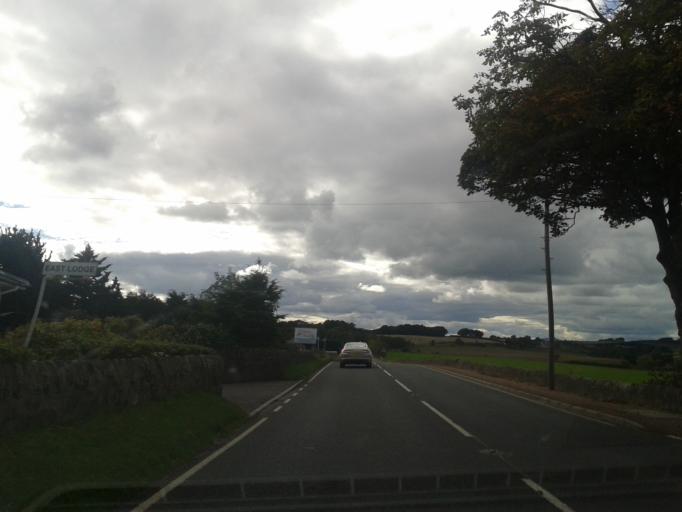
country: GB
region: Scotland
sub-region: Fife
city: Balmullo
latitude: 56.3561
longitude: -2.9224
